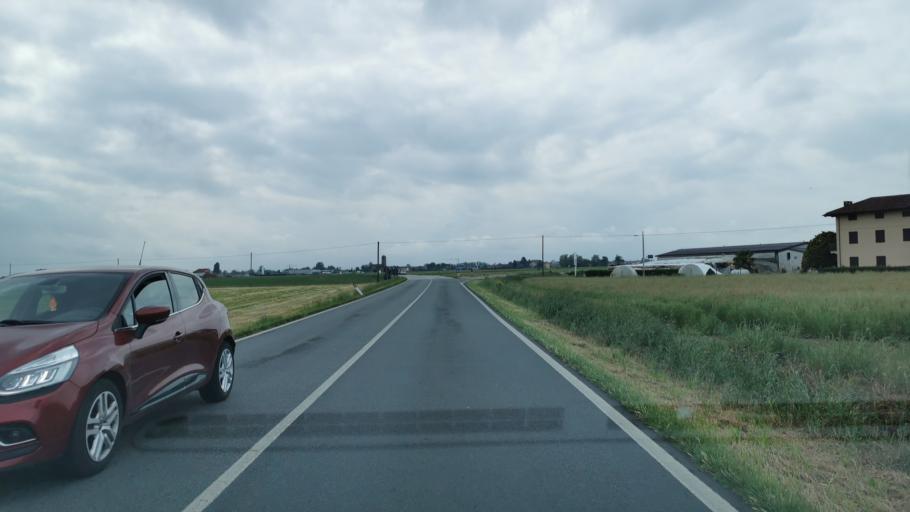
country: IT
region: Piedmont
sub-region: Provincia di Cuneo
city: Villafalletto
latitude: 44.5620
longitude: 7.5322
